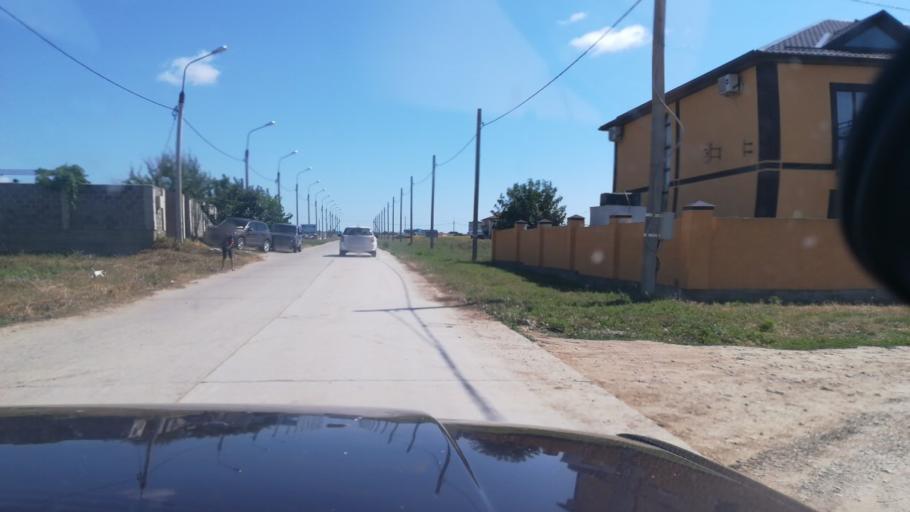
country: RU
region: Krasnodarskiy
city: Vityazevo
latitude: 44.9910
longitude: 37.2755
